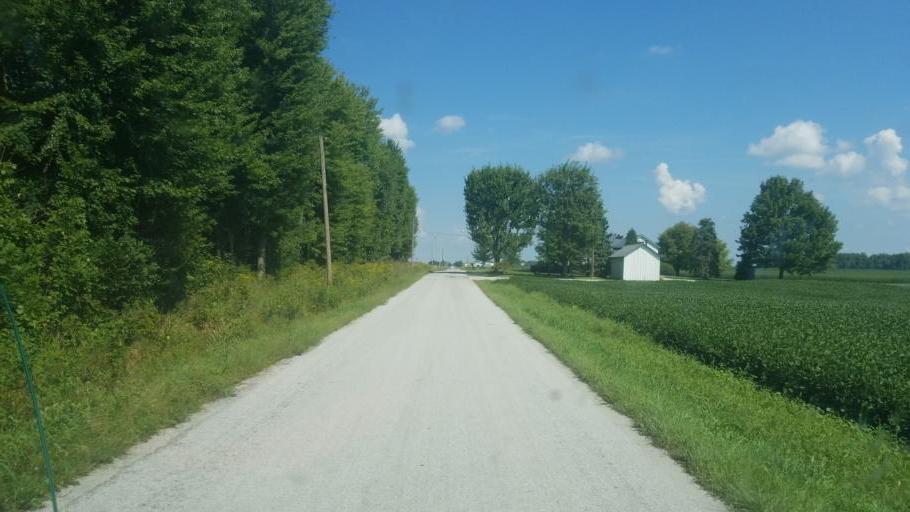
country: US
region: Ohio
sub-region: Hardin County
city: Kenton
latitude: 40.6688
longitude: -83.4957
